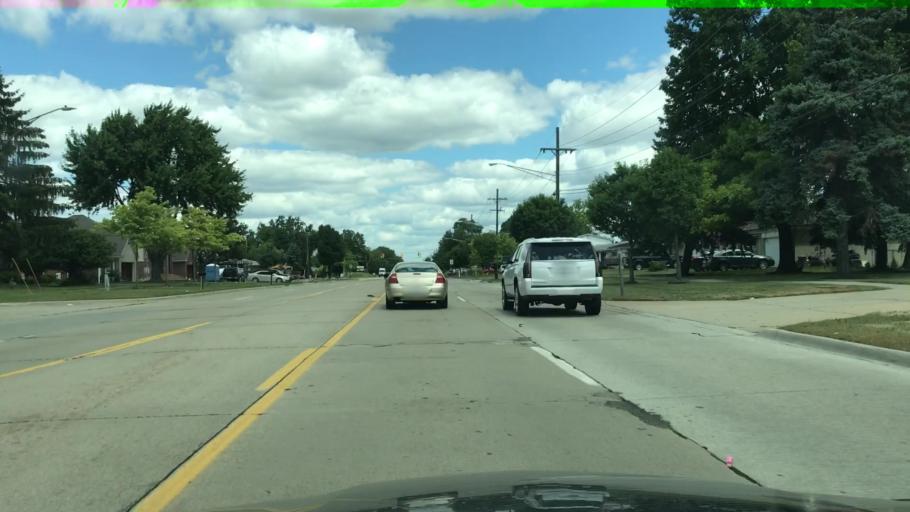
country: US
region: Michigan
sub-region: Macomb County
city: Sterling Heights
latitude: 42.5404
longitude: -83.0687
